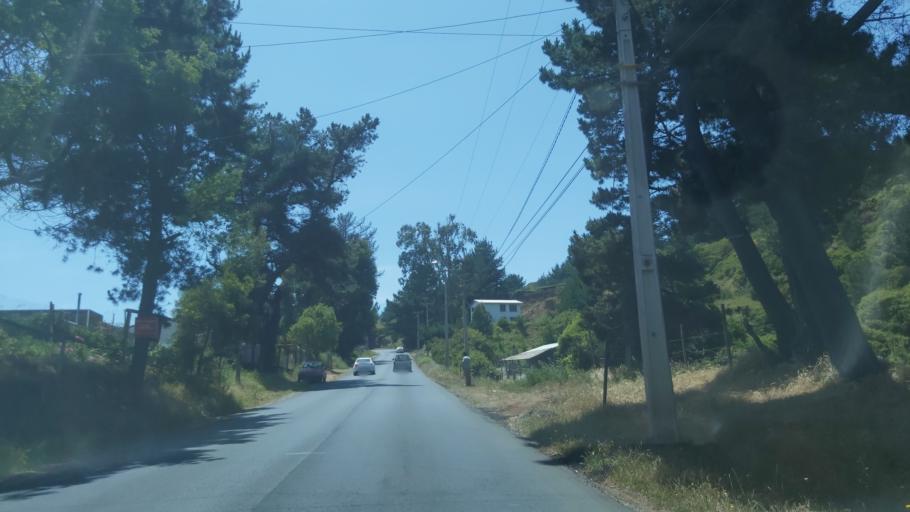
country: CL
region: Maule
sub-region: Provincia de Cauquenes
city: Cauquenes
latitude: -35.8352
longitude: -72.6224
